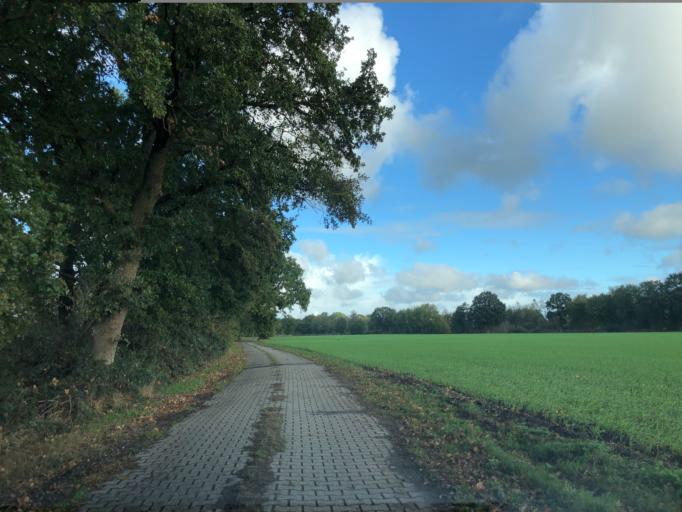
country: DE
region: Lower Saxony
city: Lehe
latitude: 53.0312
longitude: 7.3357
